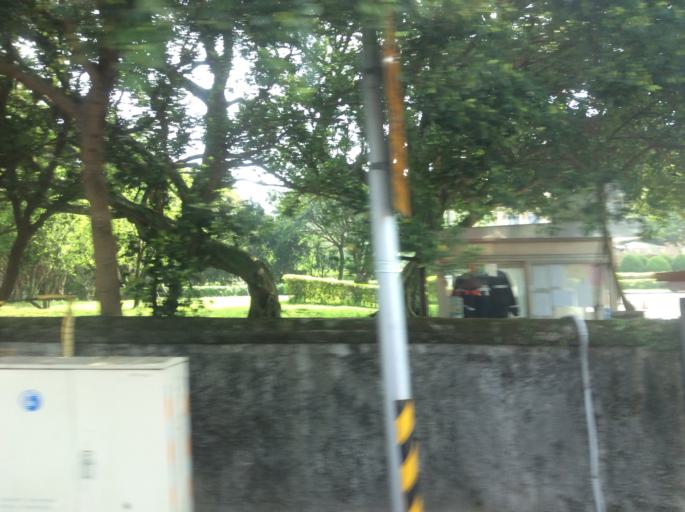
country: TW
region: Taipei
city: Taipei
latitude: 25.1391
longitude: 121.5465
